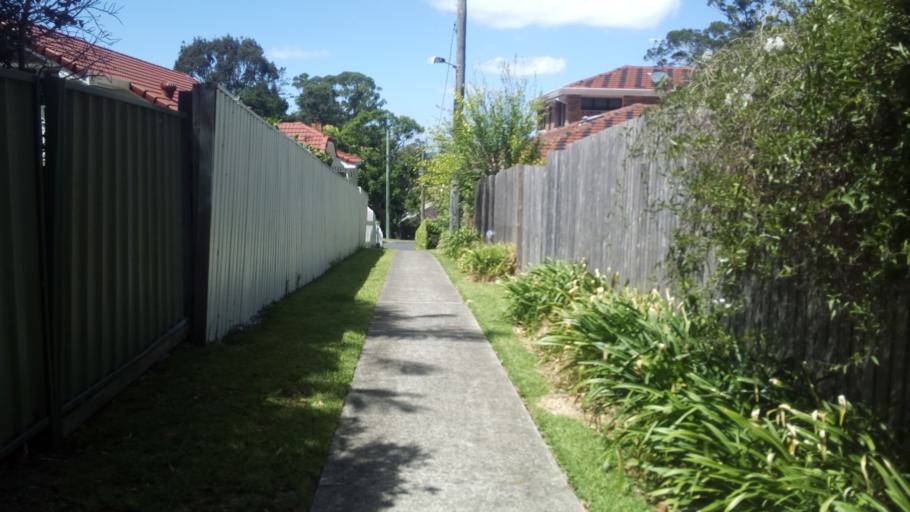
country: AU
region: New South Wales
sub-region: Wollongong
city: Mangerton
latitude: -34.4315
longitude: 150.8744
